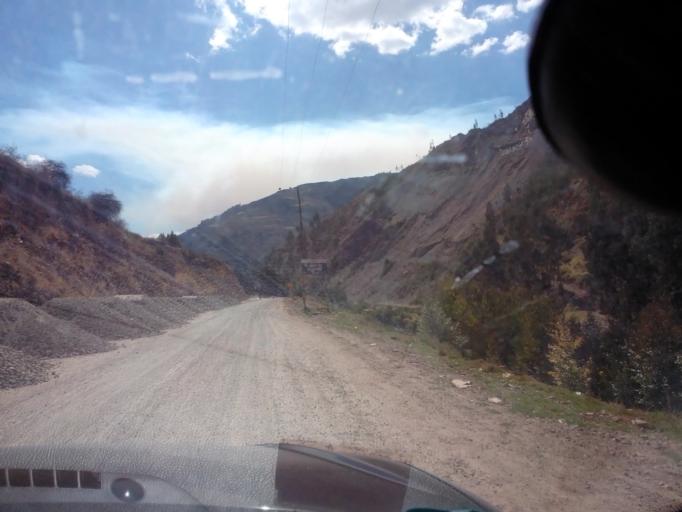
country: PE
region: Cusco
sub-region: Provincia de Anta
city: Huarocondo
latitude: -13.4112
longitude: -72.2069
